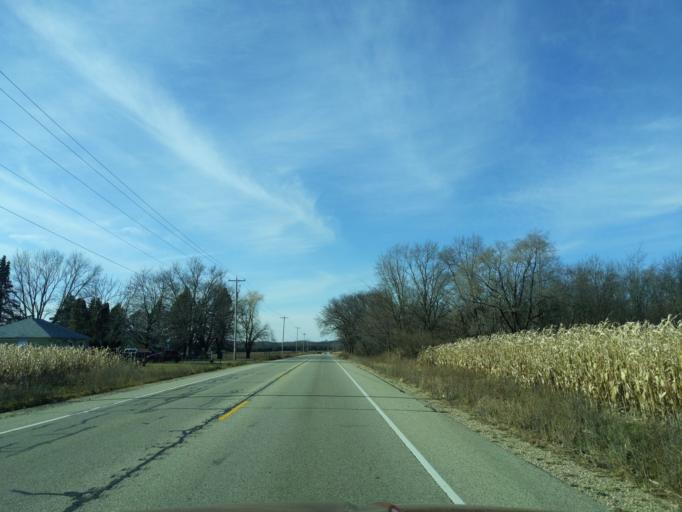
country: US
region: Wisconsin
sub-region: Jefferson County
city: Palmyra
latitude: 42.7966
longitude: -88.6307
